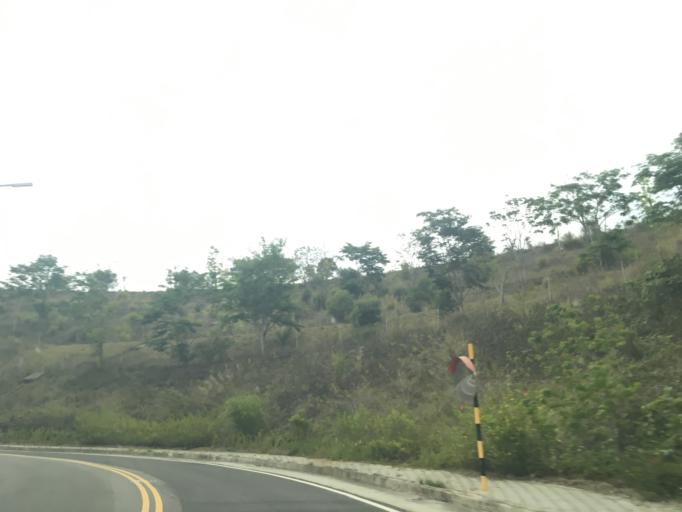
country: TW
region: Taiwan
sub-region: Taichung City
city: Taichung
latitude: 24.1742
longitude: 120.7693
